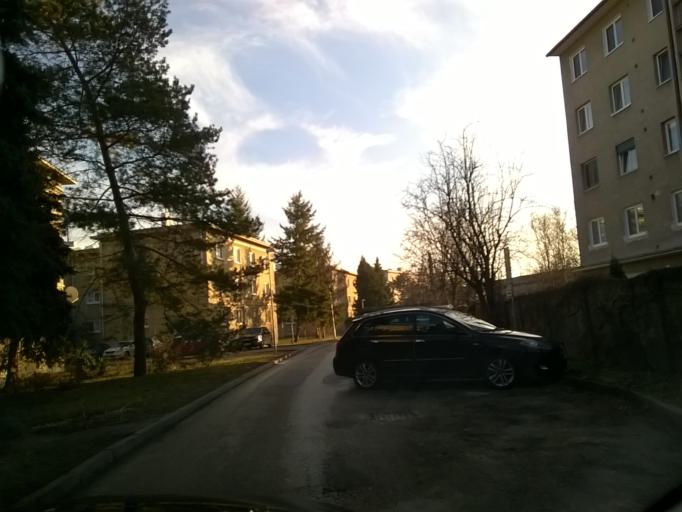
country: SK
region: Nitriansky
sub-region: Okres Nitra
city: Nitra
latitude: 48.3155
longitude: 18.0931
